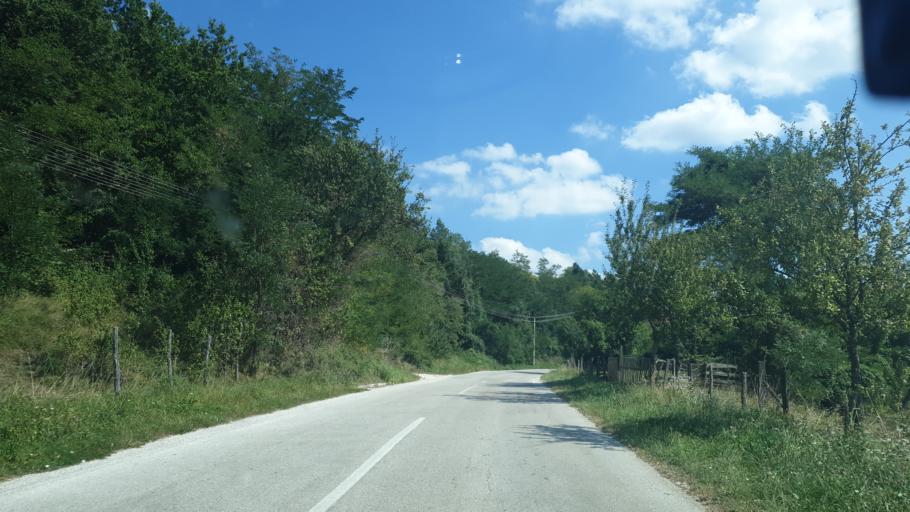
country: RS
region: Central Serbia
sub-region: Zlatiborski Okrug
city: Kosjeric
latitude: 44.0149
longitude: 20.0365
